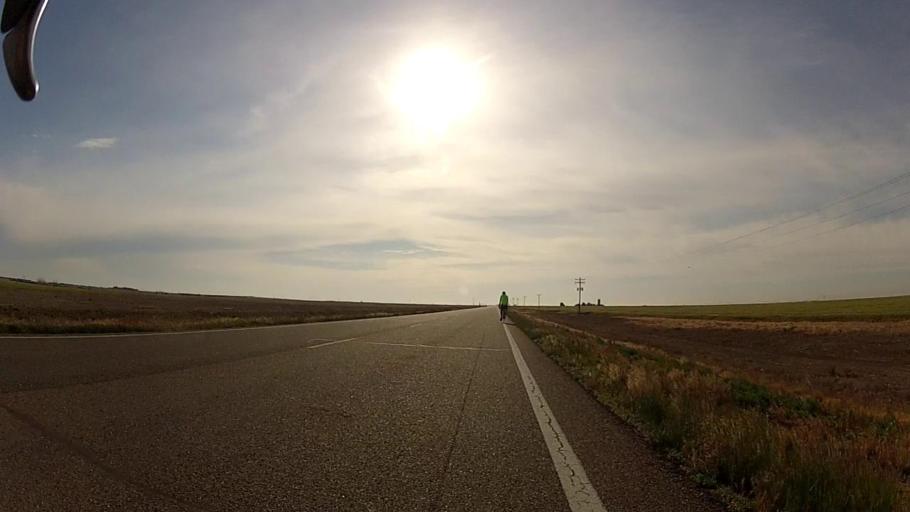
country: US
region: Kansas
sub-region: Grant County
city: Ulysses
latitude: 37.5766
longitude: -101.4593
